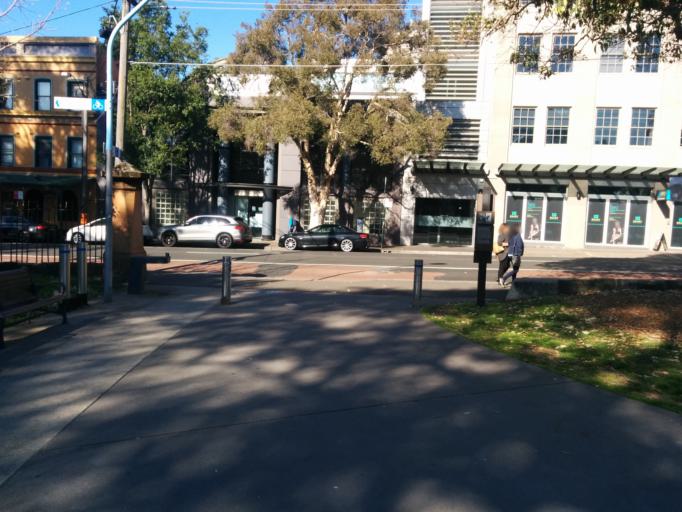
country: AU
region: New South Wales
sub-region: City of Sydney
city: Redfern
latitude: -33.8862
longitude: 151.2065
